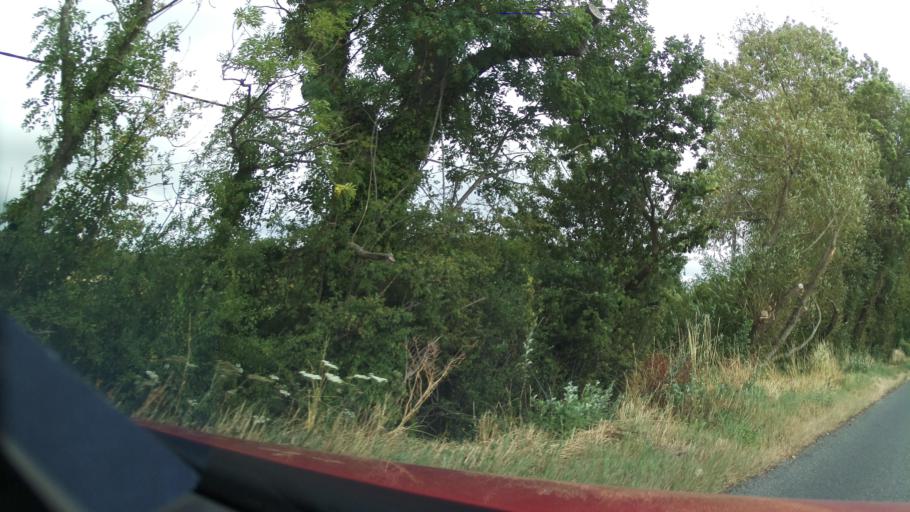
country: GB
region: England
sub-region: Derbyshire
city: Ilkeston
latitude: 52.9243
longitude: -1.3097
